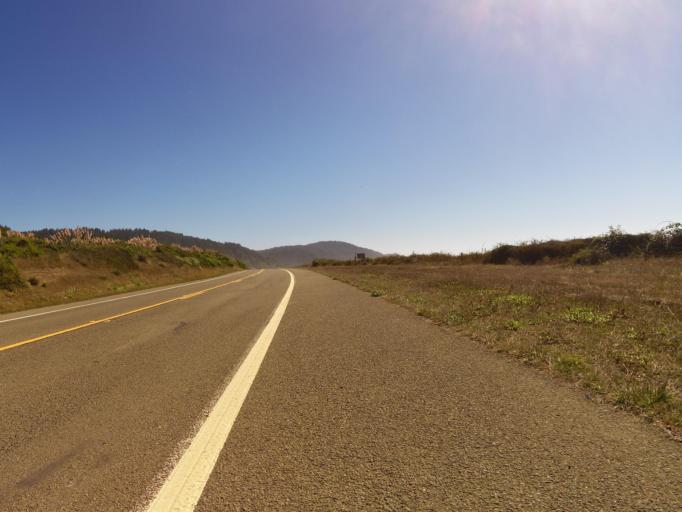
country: US
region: California
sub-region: Mendocino County
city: Fort Bragg
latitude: 39.6690
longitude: -123.7903
